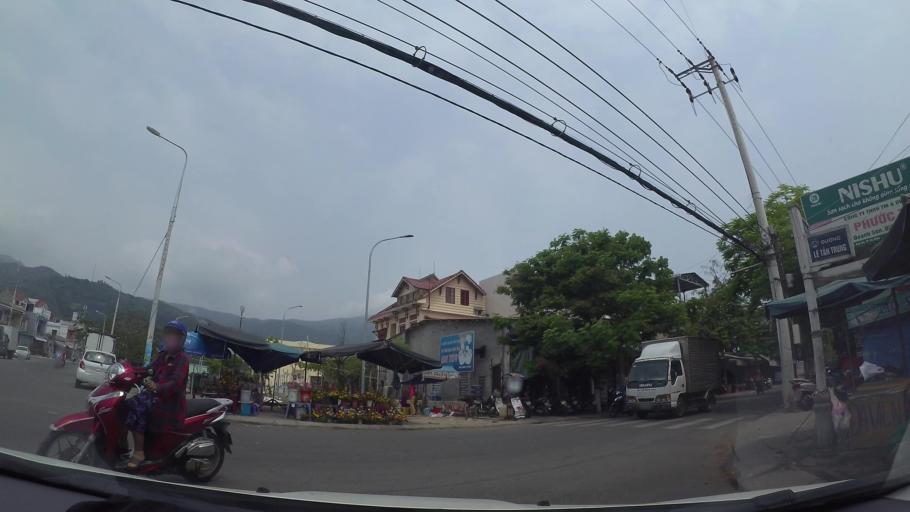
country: VN
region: Da Nang
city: Son Tra
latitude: 16.1010
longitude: 108.2498
